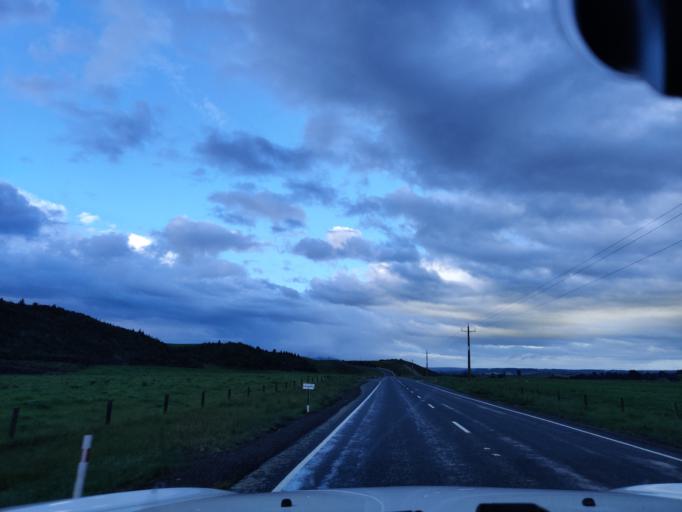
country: NZ
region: Waikato
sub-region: South Waikato District
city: Tokoroa
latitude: -38.3810
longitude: 175.7864
